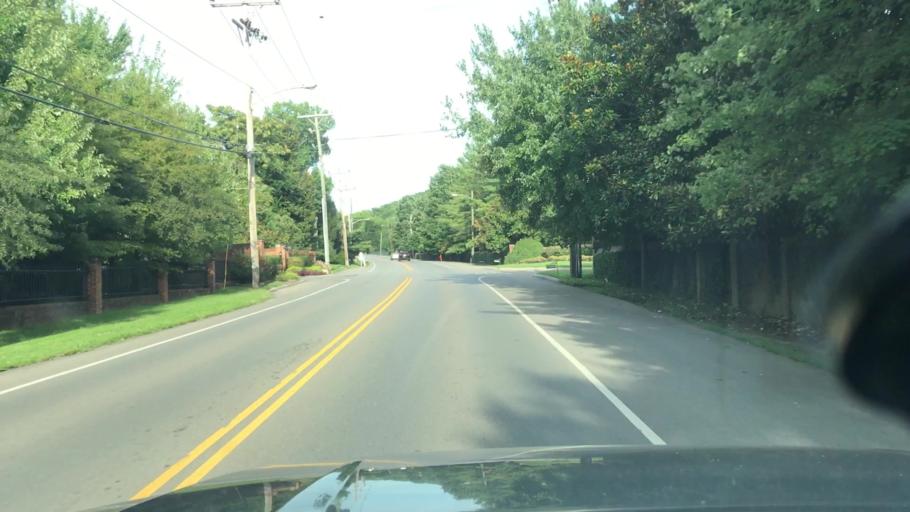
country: US
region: Tennessee
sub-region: Davidson County
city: Belle Meade
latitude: 36.0919
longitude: -86.8352
